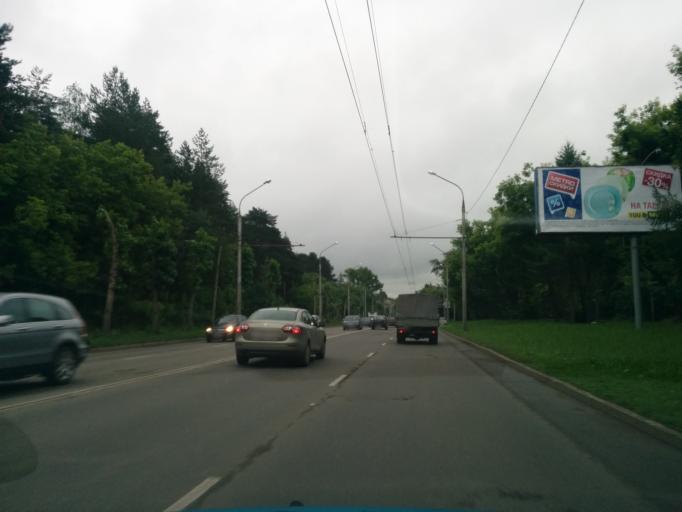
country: RU
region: Perm
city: Perm
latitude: 57.9913
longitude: 56.1841
